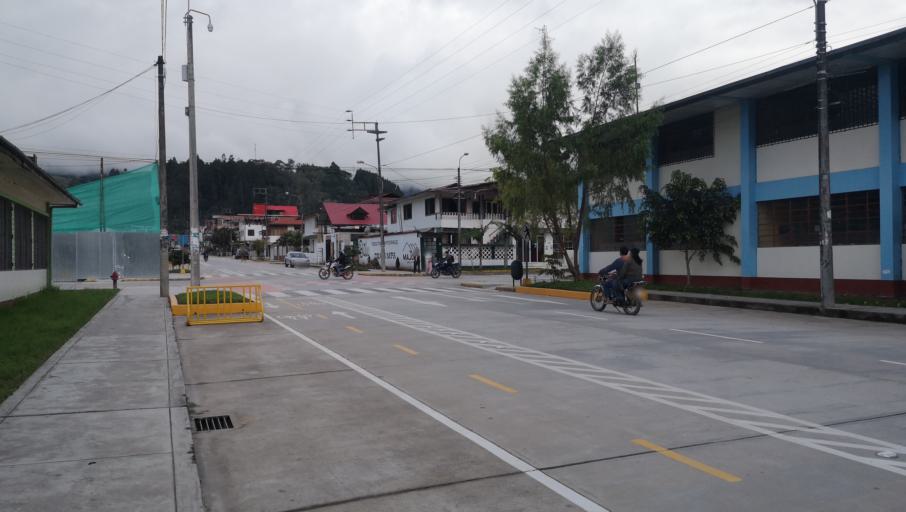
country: PE
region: Pasco
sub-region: Provincia de Oxapampa
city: Oxapampa
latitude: -10.5774
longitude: -75.4030
